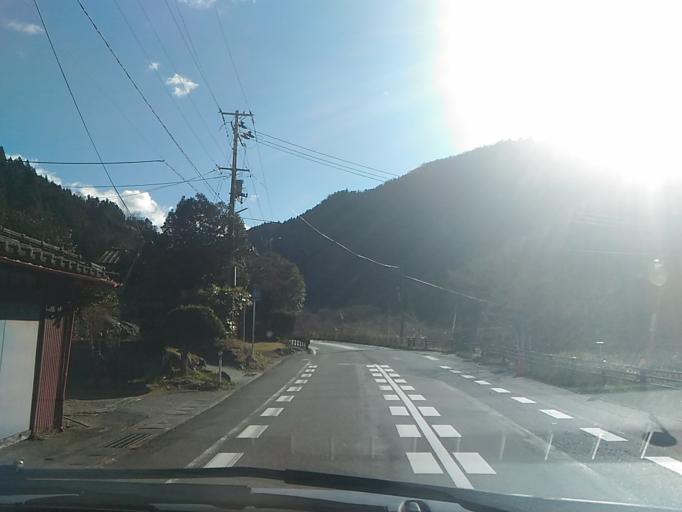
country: JP
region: Fukushima
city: Iwaki
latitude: 37.0145
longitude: 140.6723
